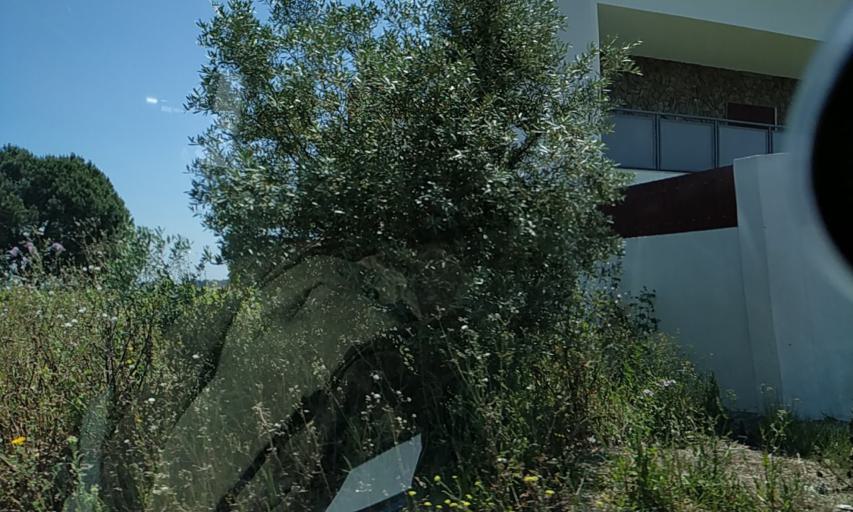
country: PT
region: Setubal
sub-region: Palmela
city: Palmela
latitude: 38.6017
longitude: -8.8045
